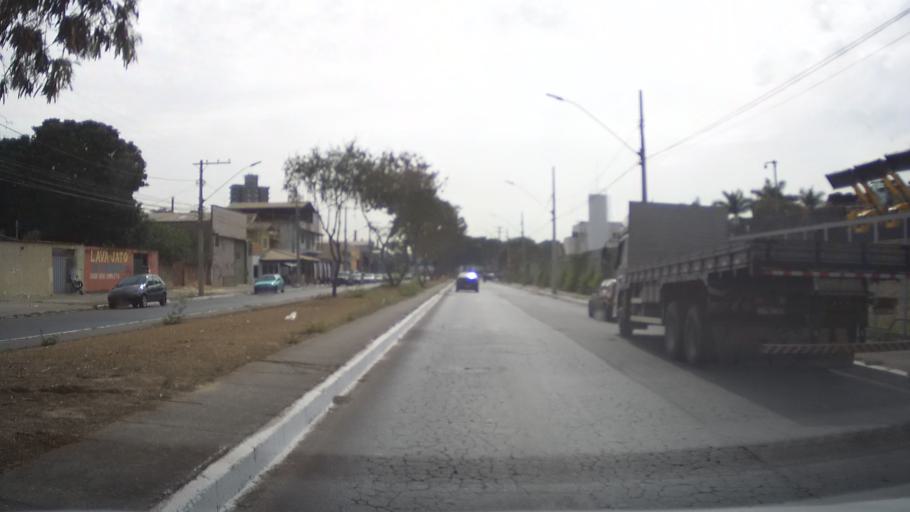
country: BR
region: Minas Gerais
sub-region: Contagem
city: Contagem
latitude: -19.9498
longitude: -44.0341
